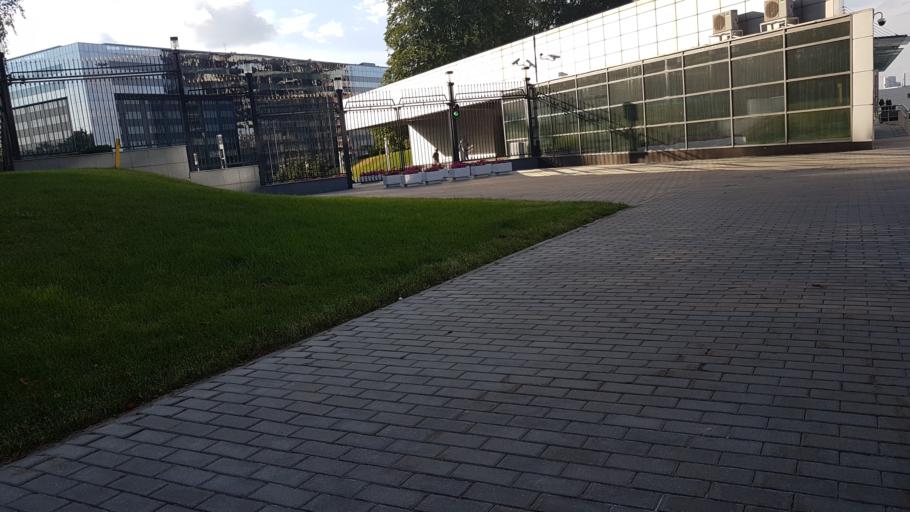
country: RU
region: Moscow
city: Strogino
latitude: 55.8143
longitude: 37.3838
